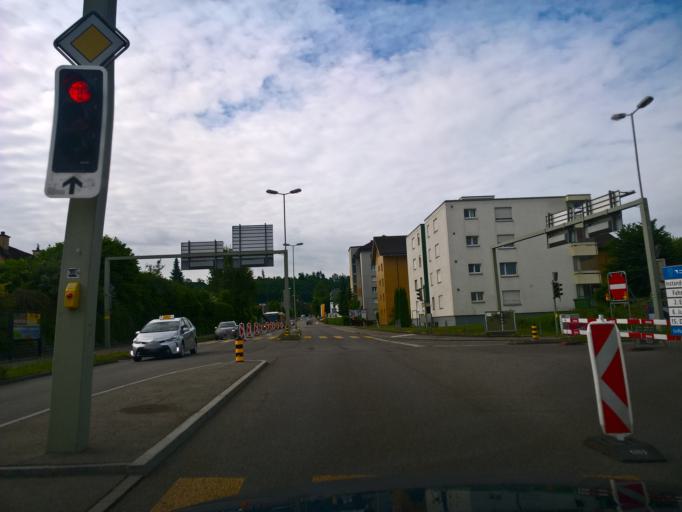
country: CH
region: Zurich
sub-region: Bezirk Buelach
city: Bachenbulach
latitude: 47.5082
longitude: 8.5448
